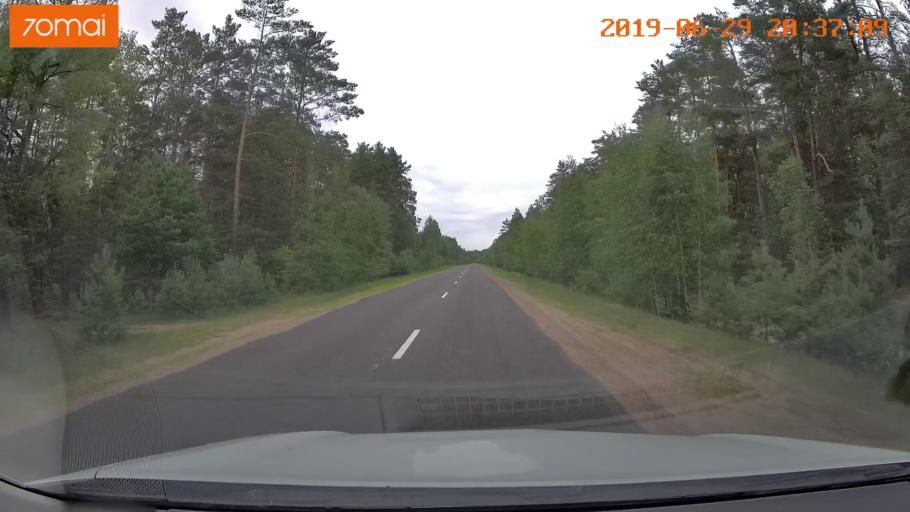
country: BY
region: Brest
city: Hantsavichy
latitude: 52.5344
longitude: 26.3633
